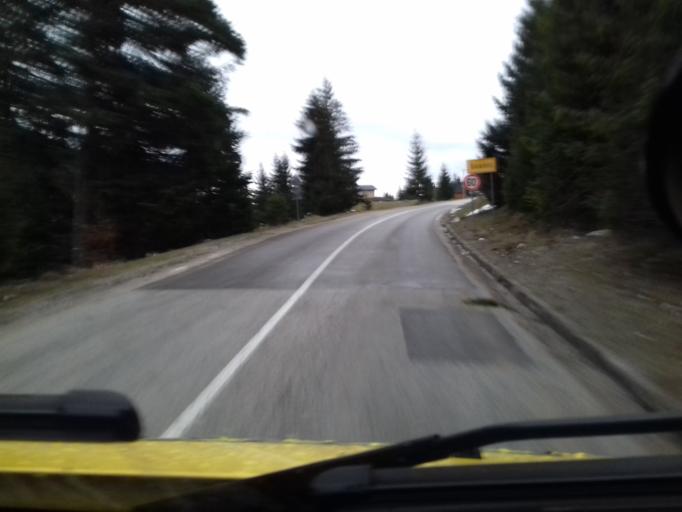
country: BA
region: Federation of Bosnia and Herzegovina
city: Turbe
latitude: 44.3045
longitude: 17.4930
